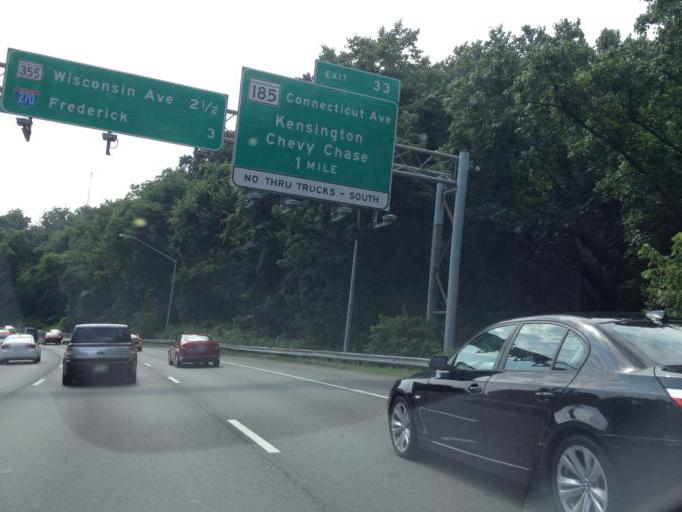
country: US
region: Maryland
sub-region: Montgomery County
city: Forest Glen
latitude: 39.0144
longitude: -77.0598
